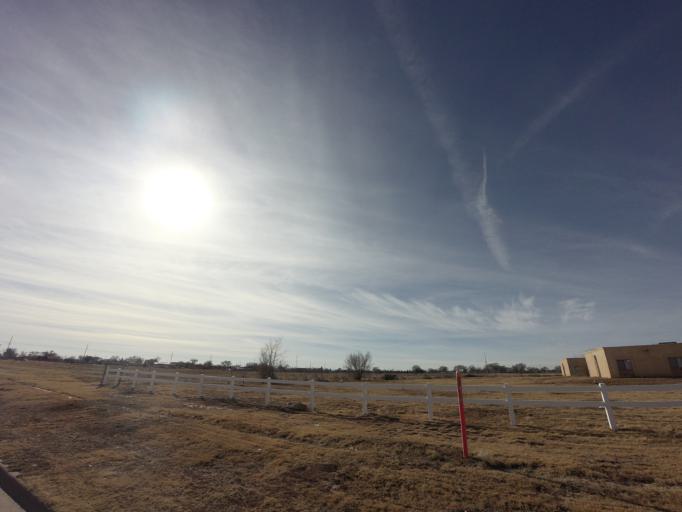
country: US
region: New Mexico
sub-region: Curry County
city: Clovis
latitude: 34.4034
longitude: -103.2230
